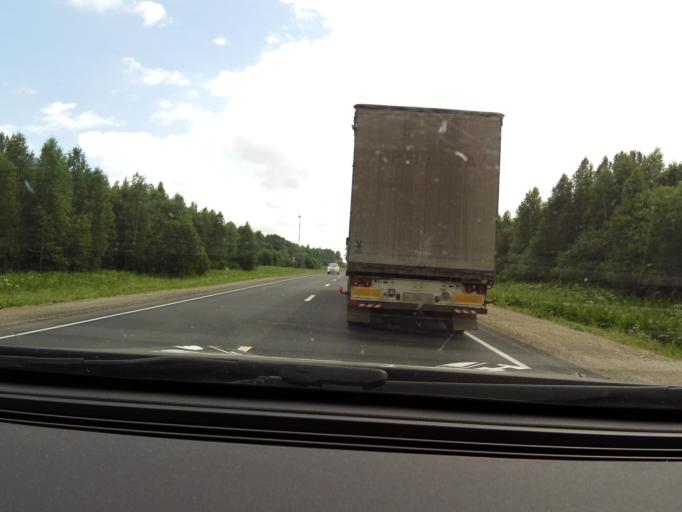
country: RU
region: Perm
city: Orda
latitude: 57.1984
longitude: 57.1100
